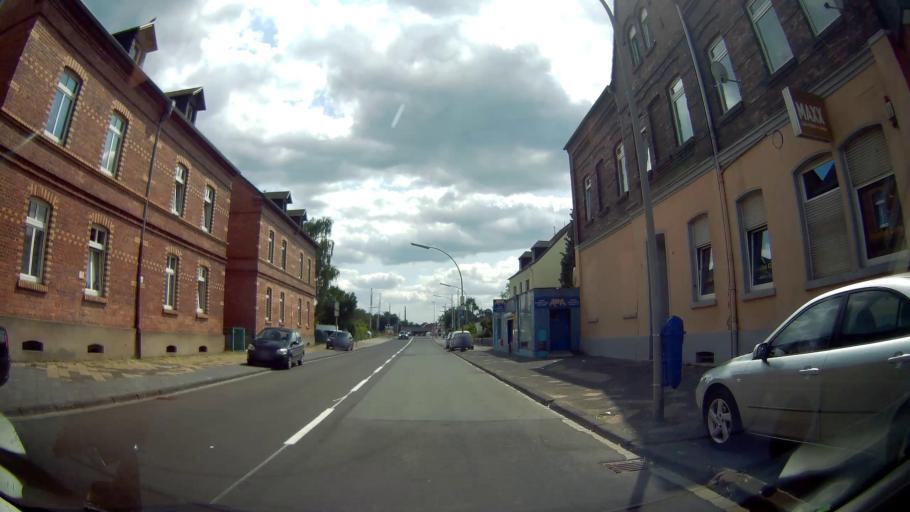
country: DE
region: North Rhine-Westphalia
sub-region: Regierungsbezirk Munster
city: Gelsenkirchen
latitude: 51.5368
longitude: 7.0865
